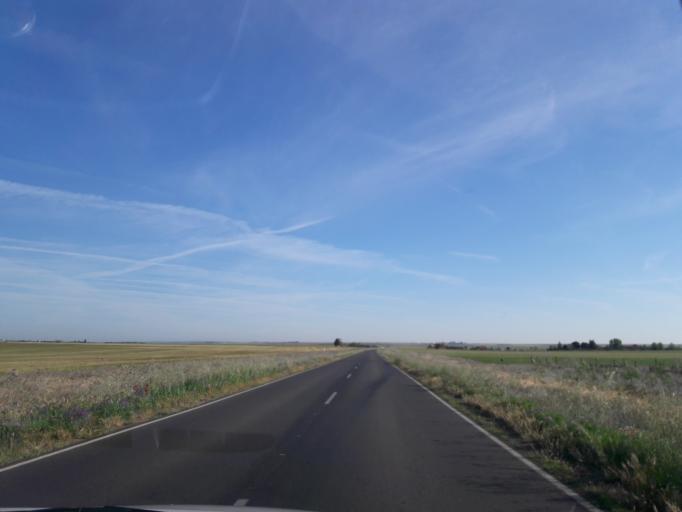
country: ES
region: Castille and Leon
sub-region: Provincia de Salamanca
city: Monterrubio de Armuna
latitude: 41.0208
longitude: -5.6506
